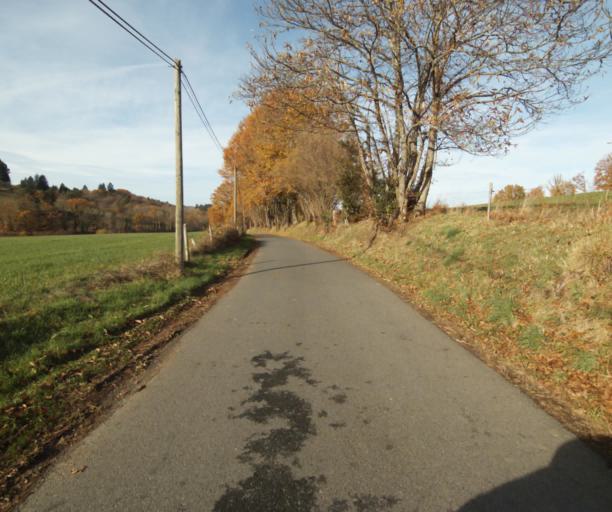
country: FR
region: Limousin
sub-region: Departement de la Correze
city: Sainte-Fortunade
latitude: 45.2117
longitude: 1.7608
